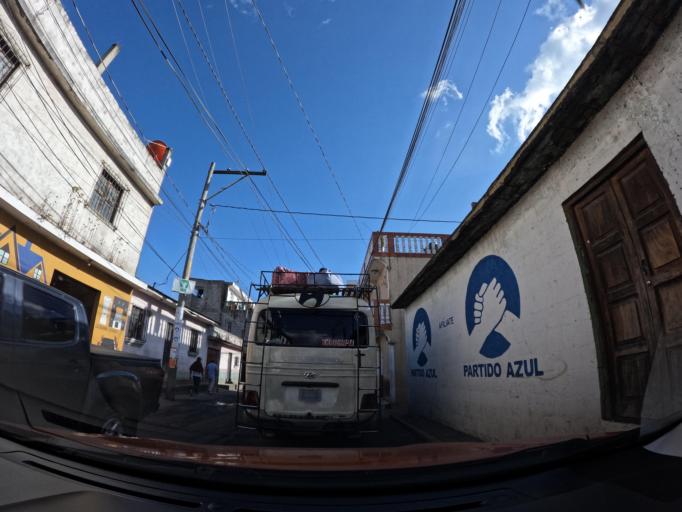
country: GT
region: Sacatepequez
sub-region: Municipio de Santa Maria de Jesus
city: Santa Maria de Jesus
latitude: 14.4975
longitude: -90.7103
